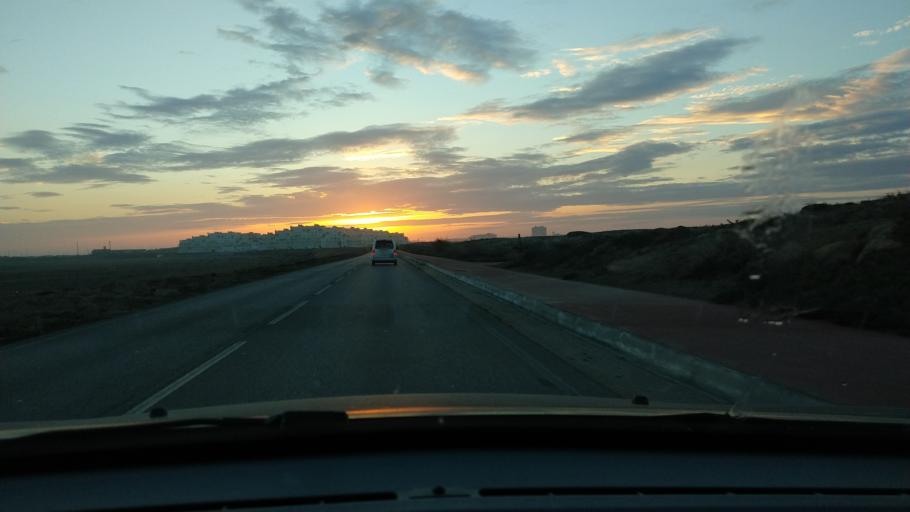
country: PT
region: Leiria
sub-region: Peniche
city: Atouguia da Baleia
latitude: 39.3579
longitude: -9.3480
